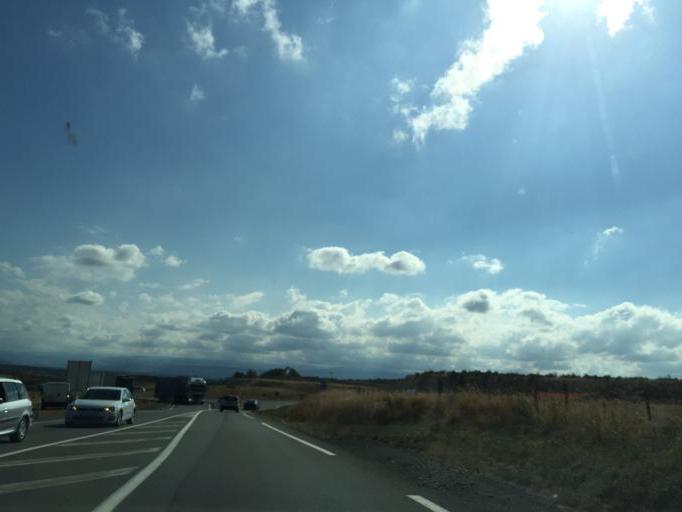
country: FR
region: Rhone-Alpes
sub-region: Departement de la Loire
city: Balbigny
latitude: 45.8447
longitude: 4.1670
